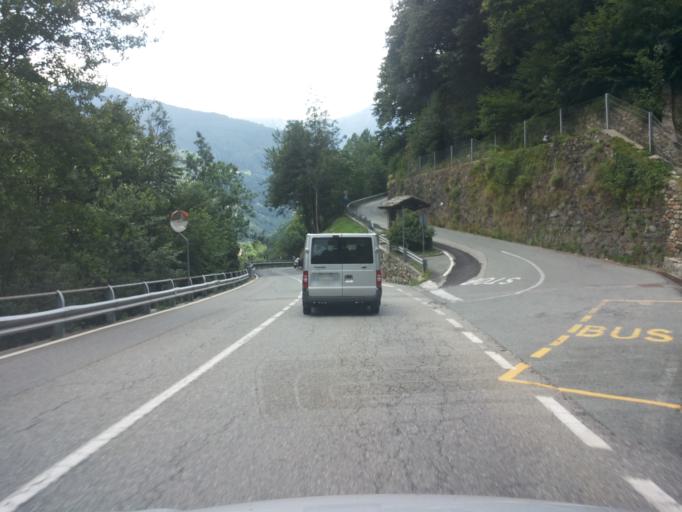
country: IT
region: Aosta Valley
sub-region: Valle d'Aosta
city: Fontainemore
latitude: 45.6665
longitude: 7.8585
